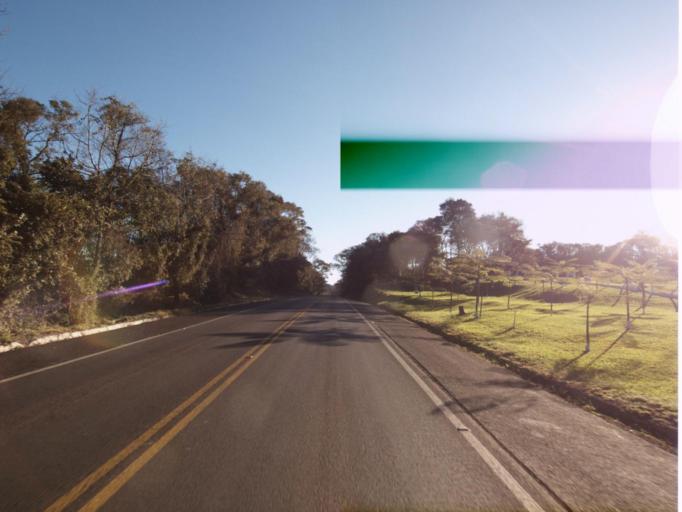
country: BR
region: Santa Catarina
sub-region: Chapeco
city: Chapeco
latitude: -26.8988
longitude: -52.8793
